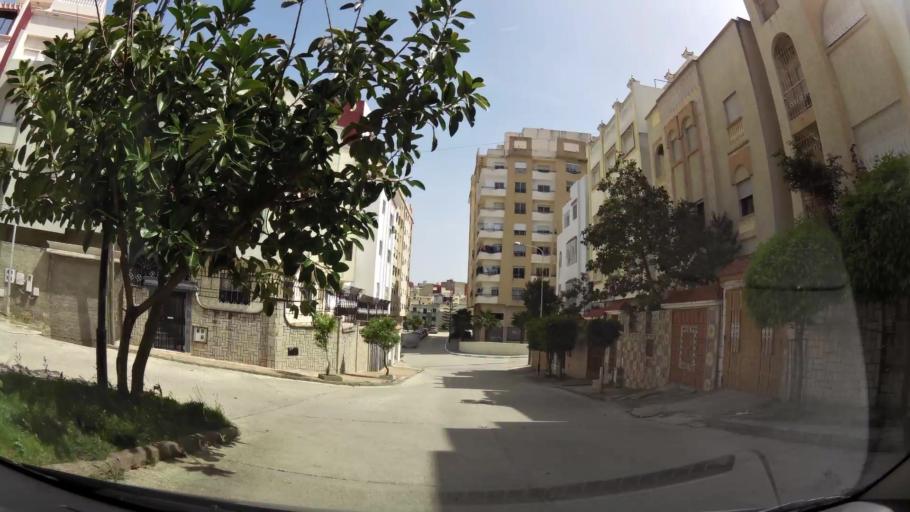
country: MA
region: Tanger-Tetouan
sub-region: Tanger-Assilah
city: Tangier
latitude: 35.7583
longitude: -5.8313
